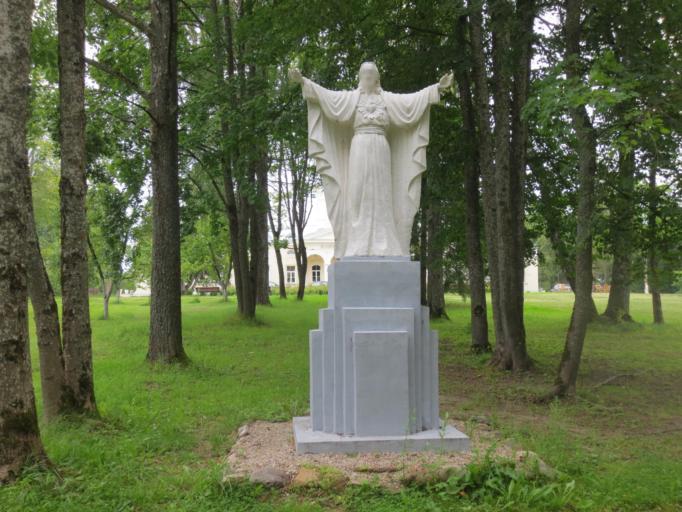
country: LT
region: Utenos apskritis
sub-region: Anyksciai
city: Anyksciai
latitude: 55.5017
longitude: 25.2180
